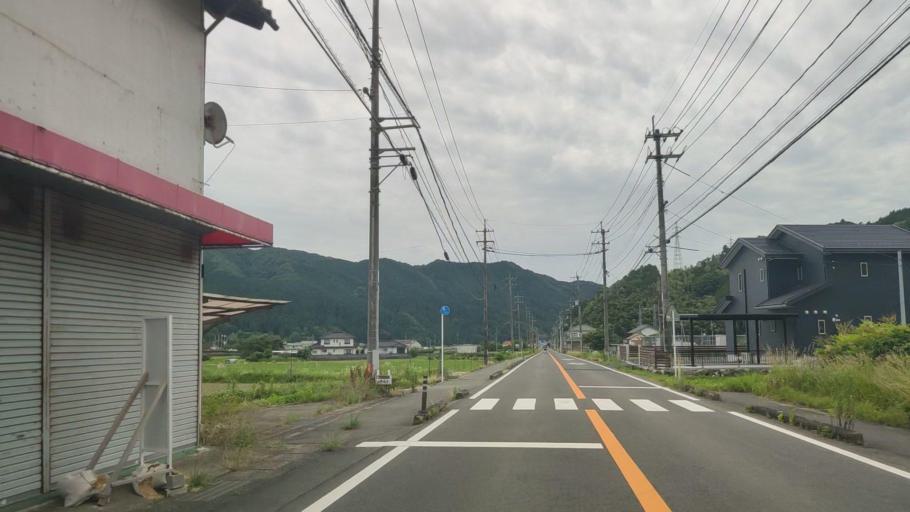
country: JP
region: Hyogo
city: Yamazakicho-nakabirose
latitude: 35.1026
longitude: 134.3250
